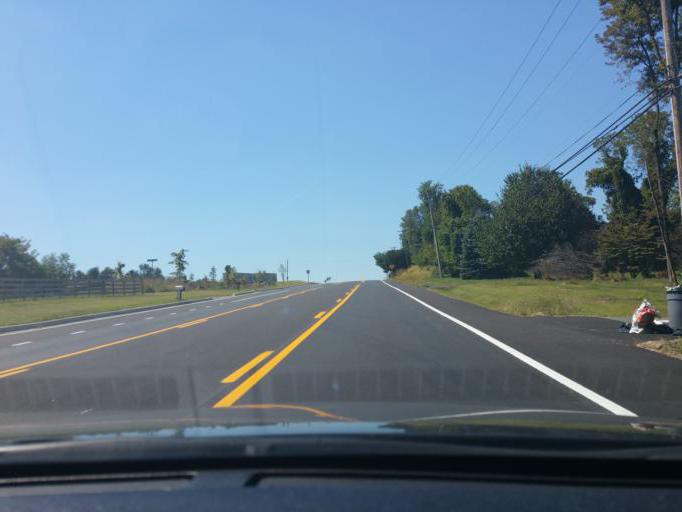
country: US
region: Maryland
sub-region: Harford County
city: Aberdeen
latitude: 39.5656
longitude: -76.2348
